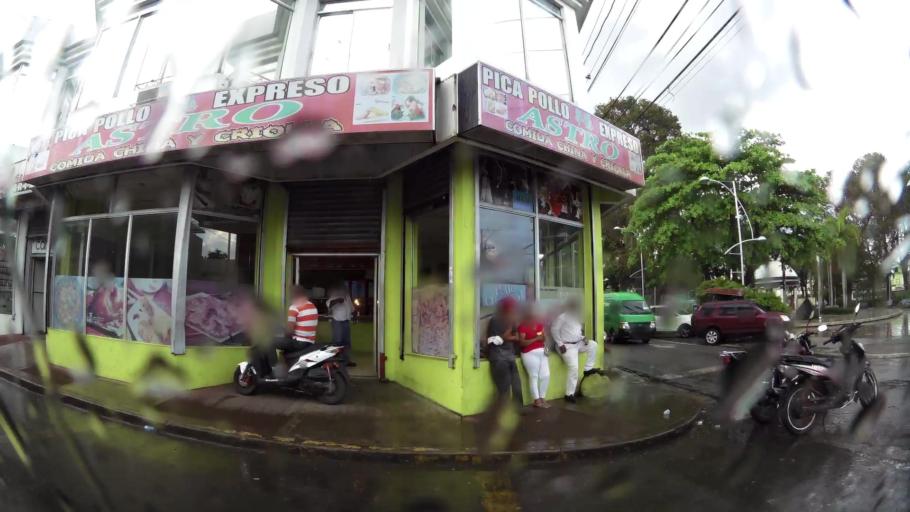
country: DO
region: Monsenor Nouel
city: Bonao
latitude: 18.9415
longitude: -70.4112
